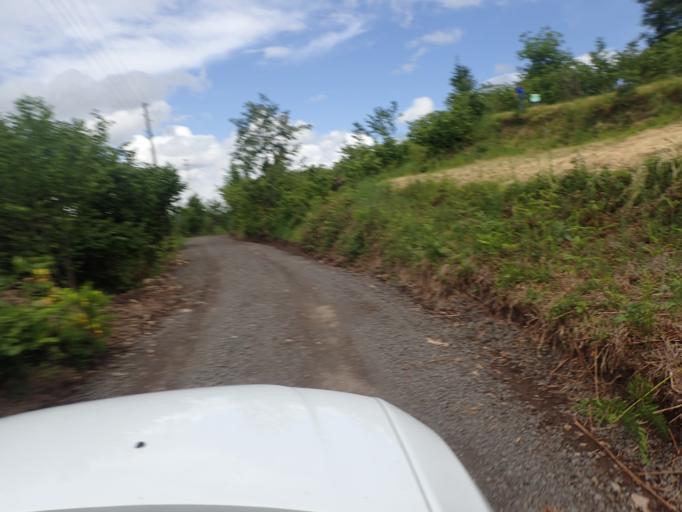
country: TR
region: Ordu
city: Akkus
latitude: 40.9162
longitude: 36.8932
